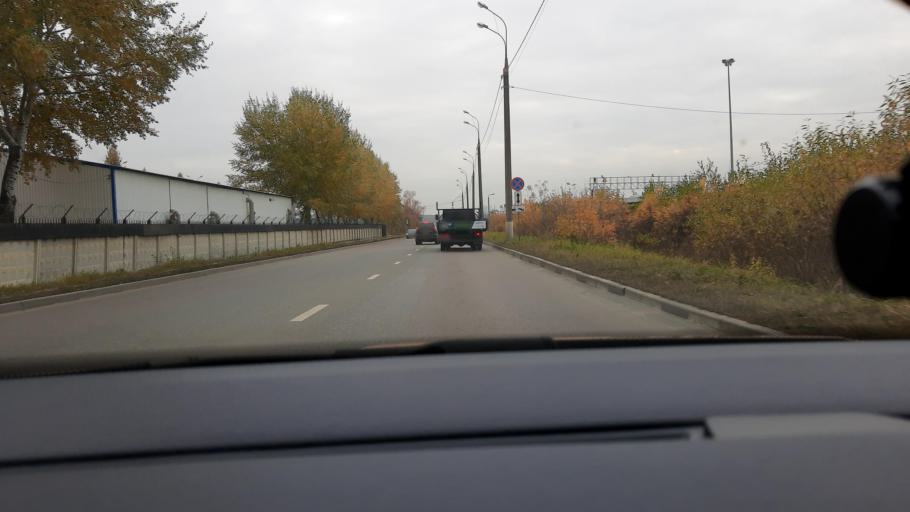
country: RU
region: Moskovskaya
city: Cherkizovo
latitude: 55.9408
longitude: 37.7646
